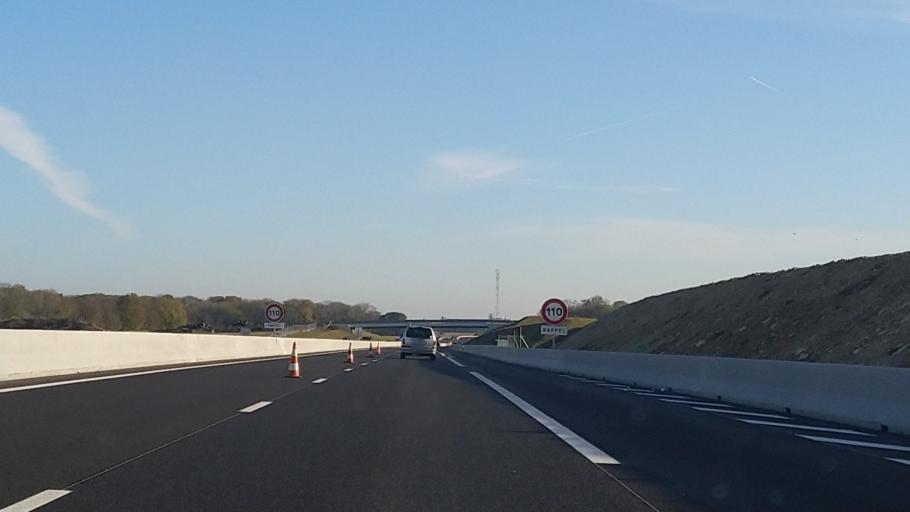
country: FR
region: Ile-de-France
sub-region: Departement du Val-d'Oise
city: Maffliers
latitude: 49.0885
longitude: 2.3122
